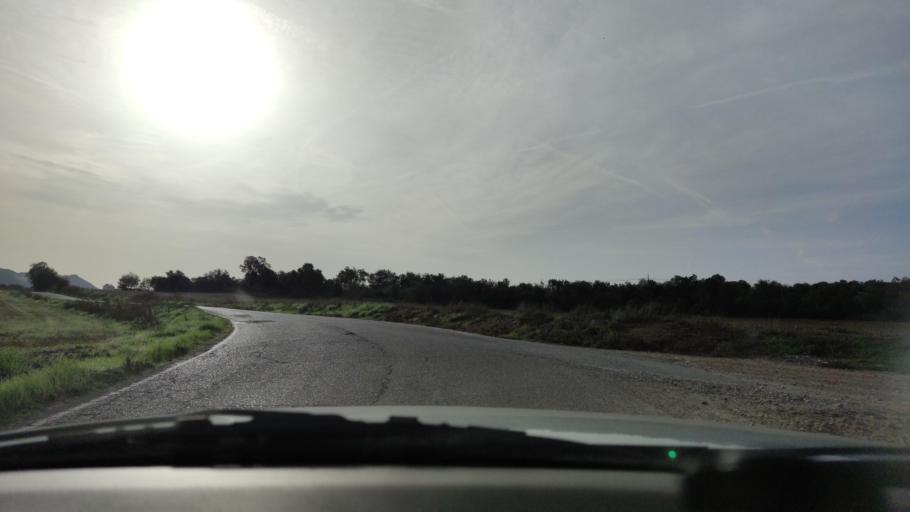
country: ES
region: Catalonia
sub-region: Provincia de Lleida
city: Artesa de Segre
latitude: 41.9086
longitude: 1.0356
